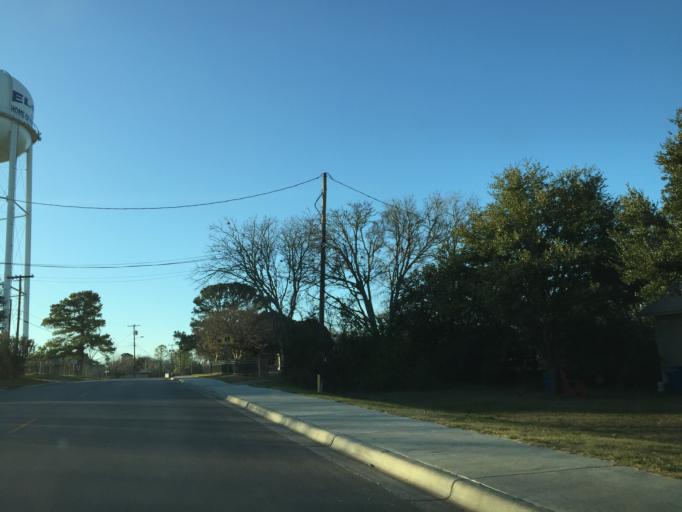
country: US
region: Texas
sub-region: Bastrop County
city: Elgin
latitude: 30.3475
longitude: -97.3771
